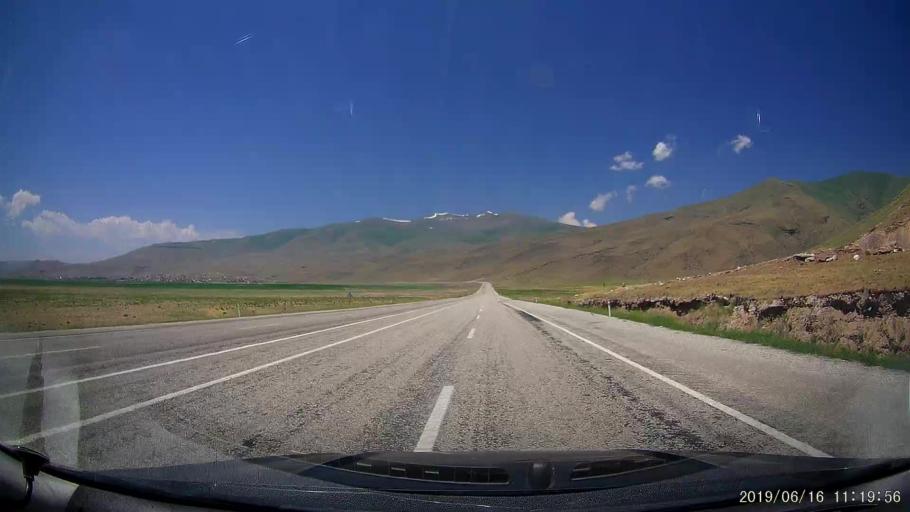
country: TR
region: Agri
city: Dogubayazit
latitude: 39.6962
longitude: 44.1030
